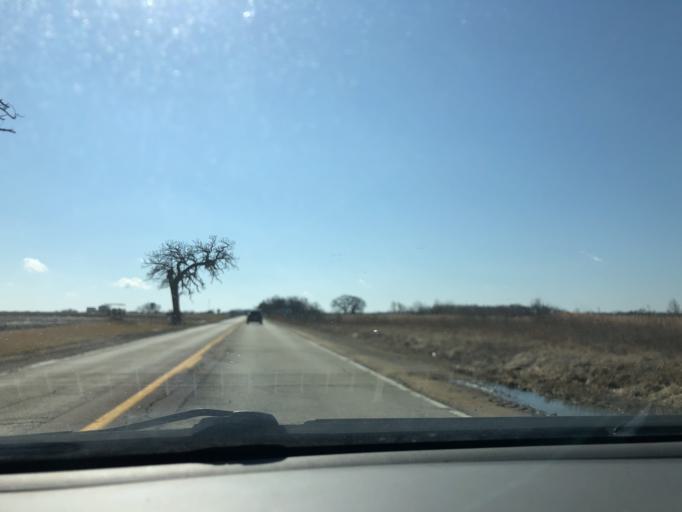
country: US
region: Illinois
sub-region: Kane County
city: Pingree Grove
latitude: 42.1028
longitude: -88.4547
